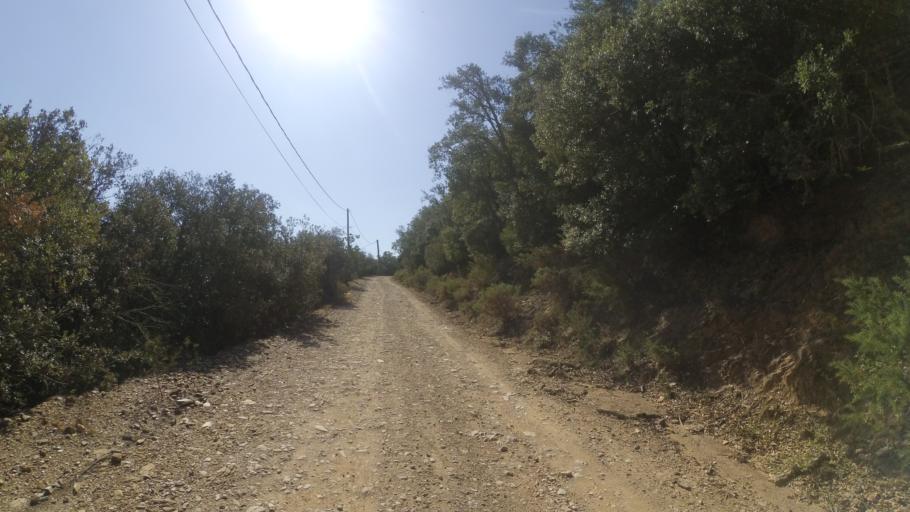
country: FR
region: Languedoc-Roussillon
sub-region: Departement des Pyrenees-Orientales
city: Millas
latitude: 42.6215
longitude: 2.6761
